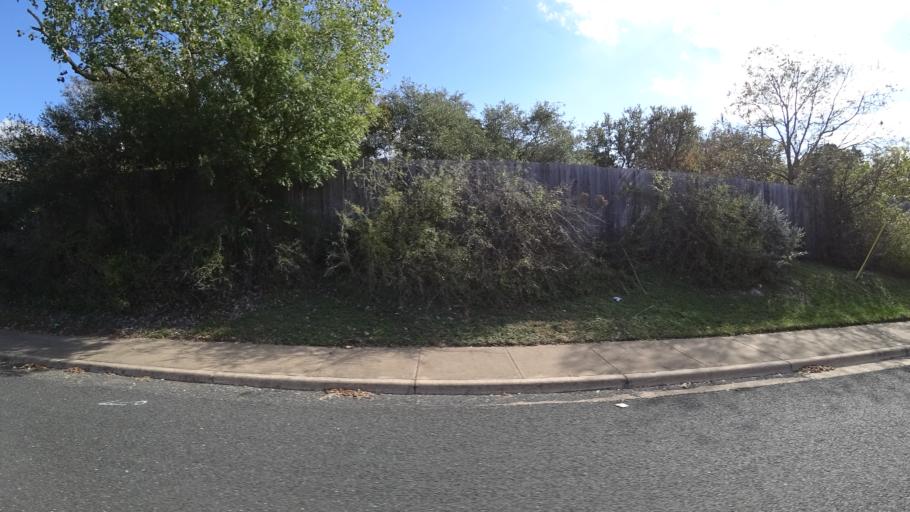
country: US
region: Texas
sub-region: Williamson County
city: Jollyville
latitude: 30.4226
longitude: -97.7862
